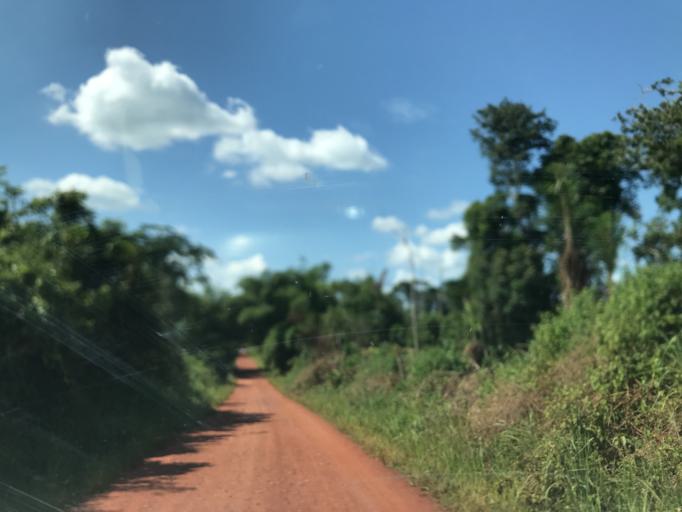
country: CD
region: Eastern Province
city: Kisangani
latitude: 1.2099
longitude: 25.2646
